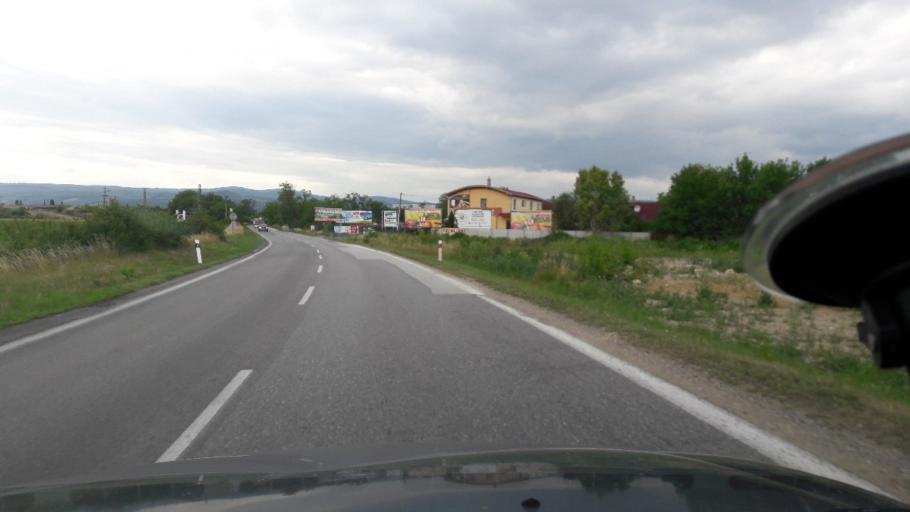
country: SK
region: Bratislavsky
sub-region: Okres Pezinok
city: Pezinok
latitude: 48.2819
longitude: 17.2912
